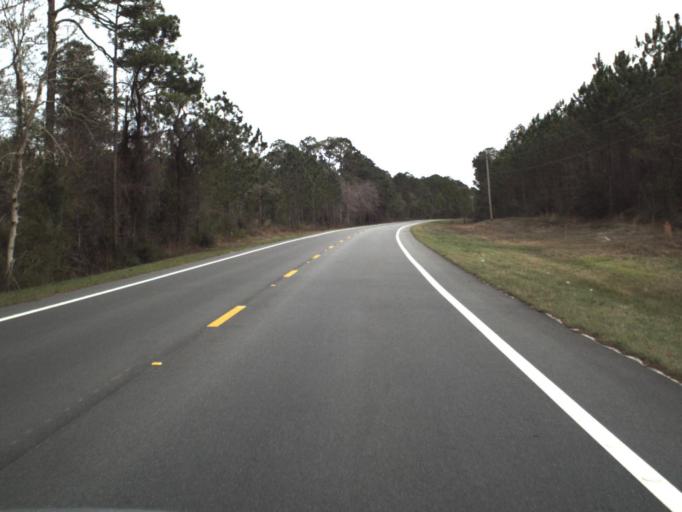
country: US
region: Florida
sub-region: Gulf County
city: Wewahitchka
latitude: 30.1381
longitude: -85.2470
